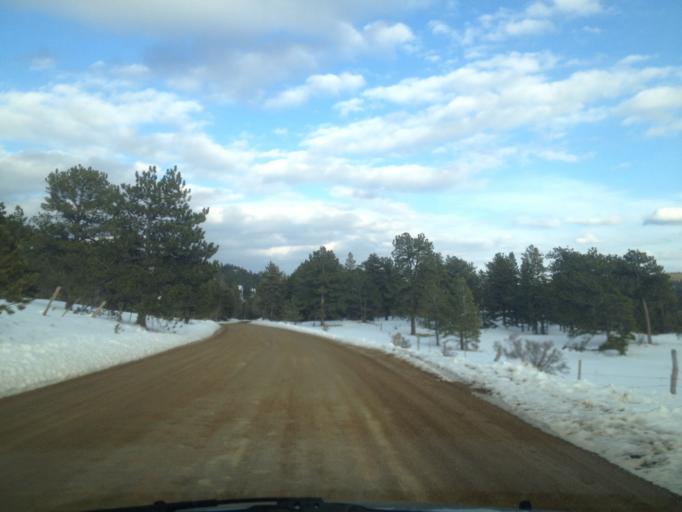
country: US
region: Colorado
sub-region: Boulder County
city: Nederland
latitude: 40.1257
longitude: -105.4730
